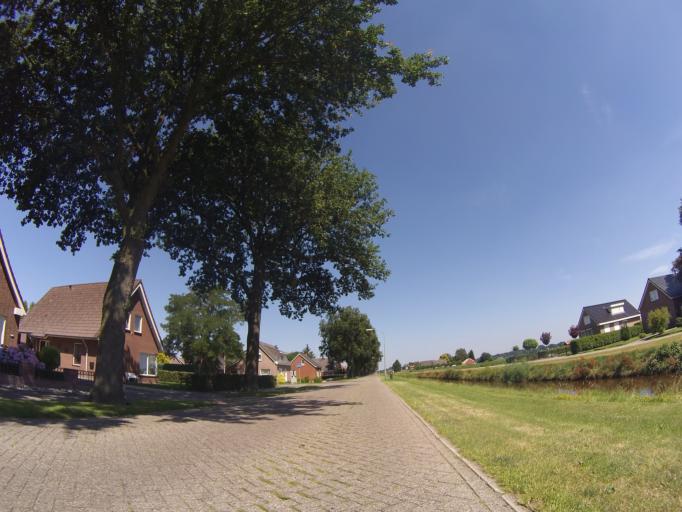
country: NL
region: Drenthe
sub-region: Gemeente Emmen
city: Klazienaveen
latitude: 52.7123
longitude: 7.0462
